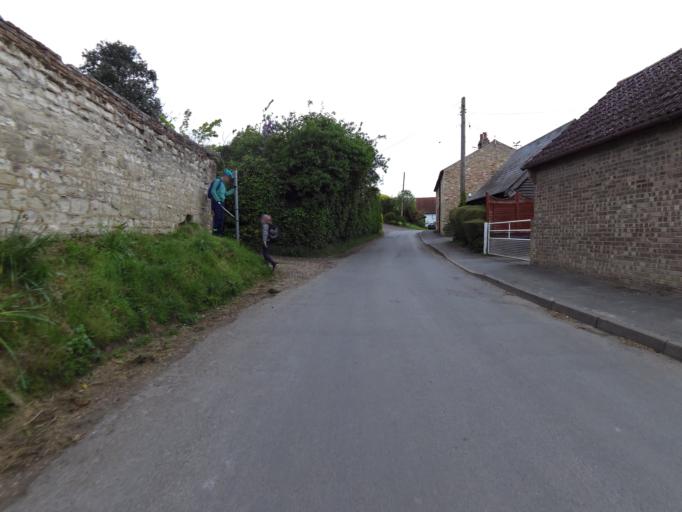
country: GB
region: England
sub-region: Cambridgeshire
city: Bottisham
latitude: 52.2719
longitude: 0.2934
